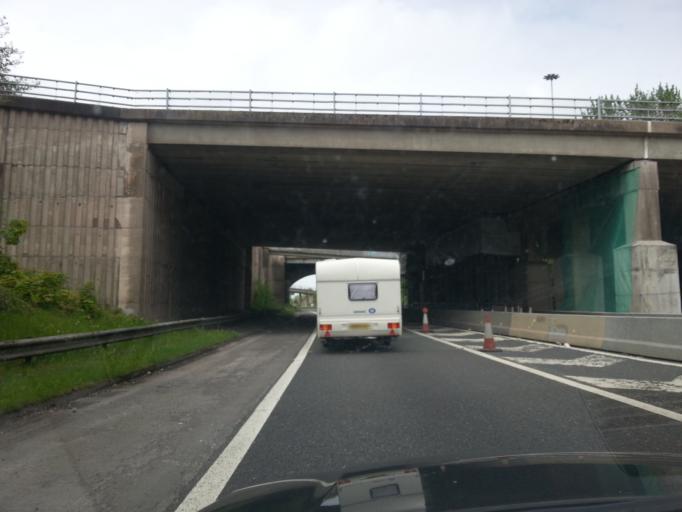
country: GB
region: England
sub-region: Borough of Halton
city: Runcorn
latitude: 53.3401
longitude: -2.7382
